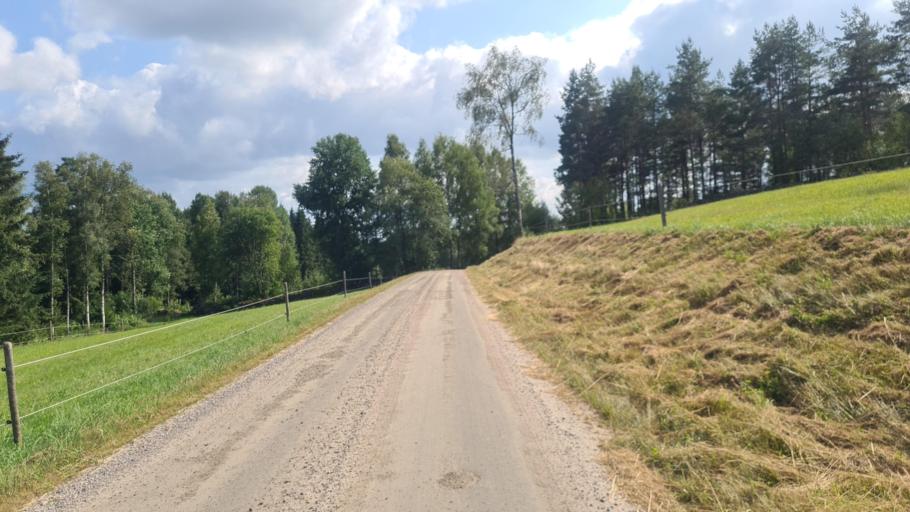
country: SE
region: Kronoberg
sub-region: Ljungby Kommun
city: Ljungby
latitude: 56.7203
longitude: 13.8812
